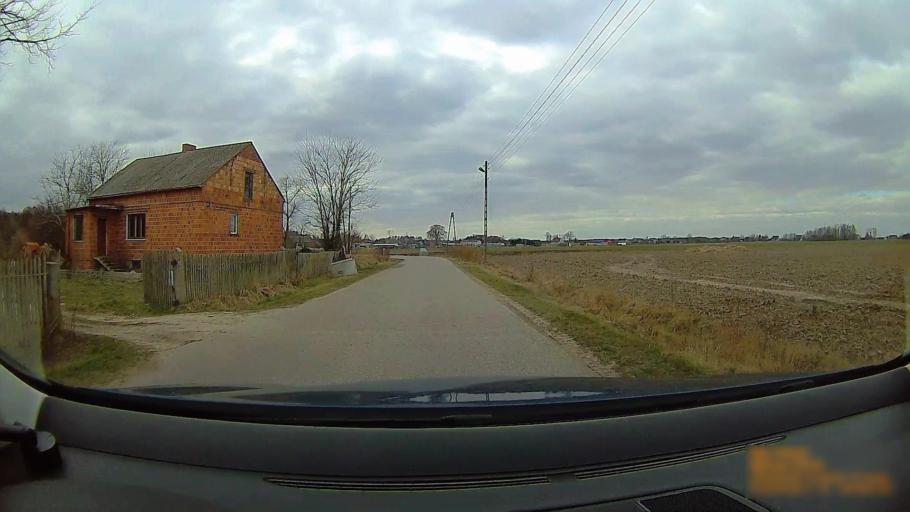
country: PL
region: Greater Poland Voivodeship
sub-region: Powiat koninski
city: Rzgow Pierwszy
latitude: 52.1295
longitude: 18.0676
